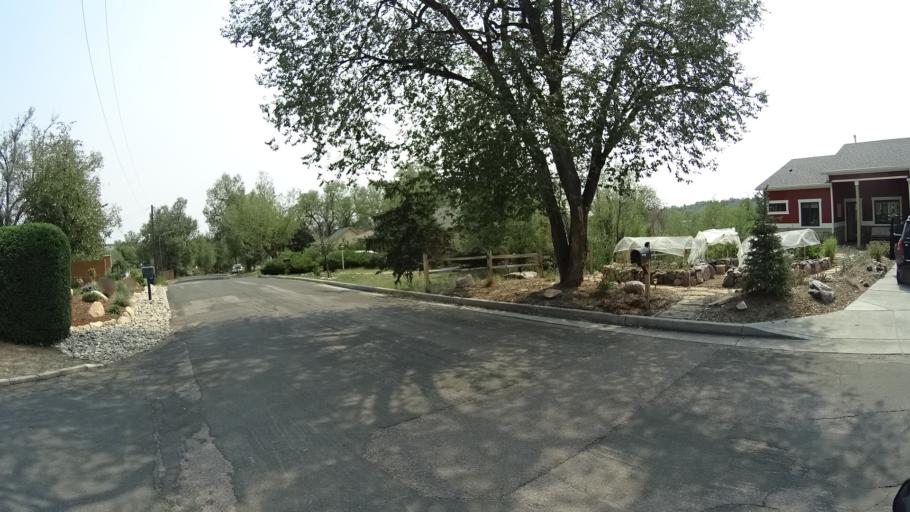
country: US
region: Colorado
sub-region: El Paso County
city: Colorado Springs
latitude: 38.8114
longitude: -104.8299
